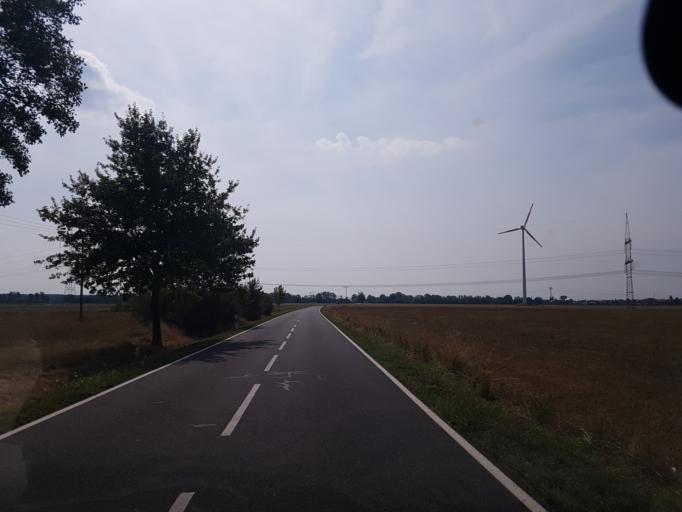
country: DE
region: Brandenburg
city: Finsterwalde
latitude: 51.6555
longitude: 13.7345
